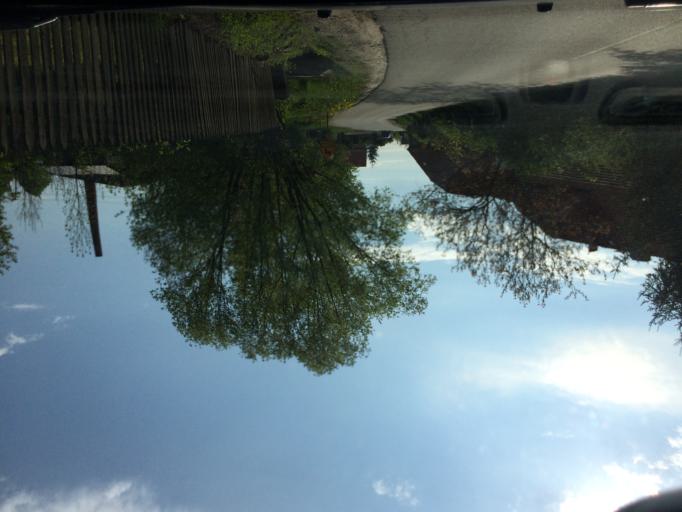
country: PL
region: Lower Silesian Voivodeship
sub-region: Powiat dzierzoniowski
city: Pieszyce
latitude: 50.7573
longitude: 16.5372
